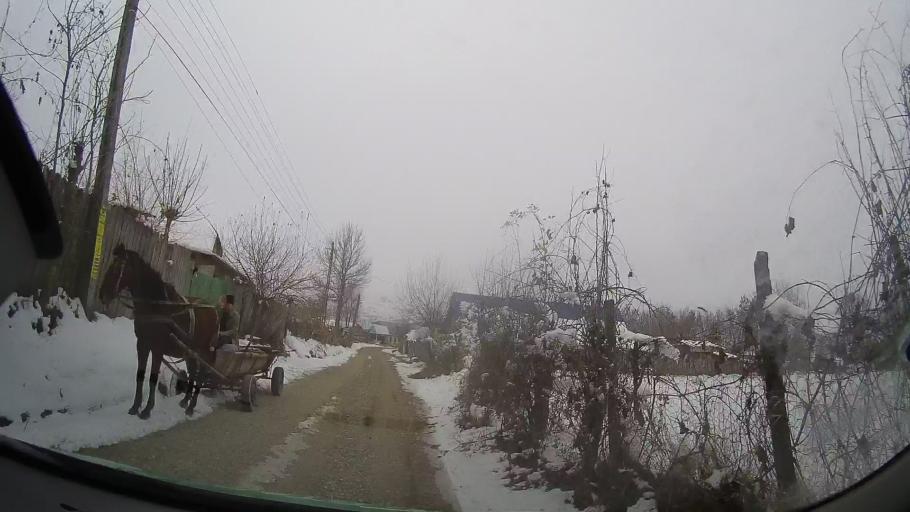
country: RO
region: Bacau
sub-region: Comuna Vultureni
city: Vultureni
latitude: 46.3714
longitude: 27.2833
